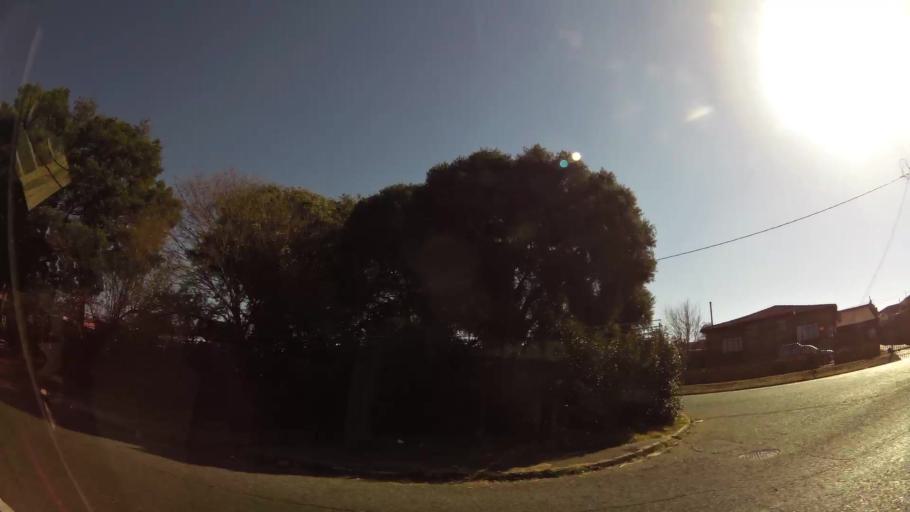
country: ZA
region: Gauteng
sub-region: City of Johannesburg Metropolitan Municipality
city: Johannesburg
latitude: -26.1943
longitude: 27.9873
